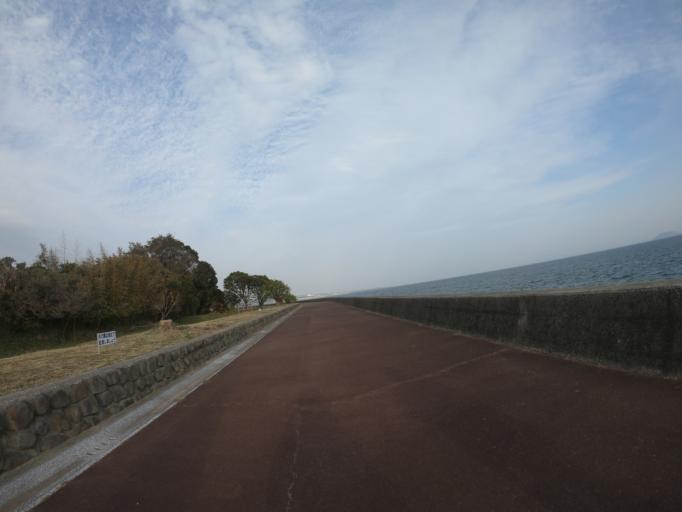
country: JP
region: Nagasaki
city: Shimabara
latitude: 32.6325
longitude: 130.2585
